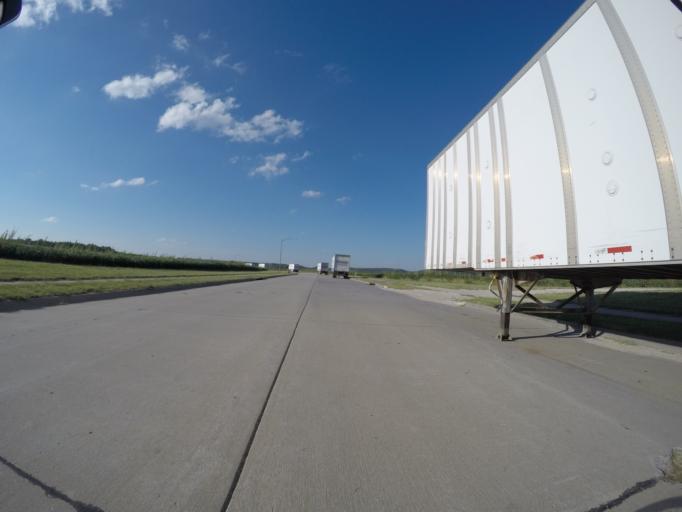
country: US
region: Kansas
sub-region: Riley County
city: Ogden
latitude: 39.1424
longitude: -96.6770
